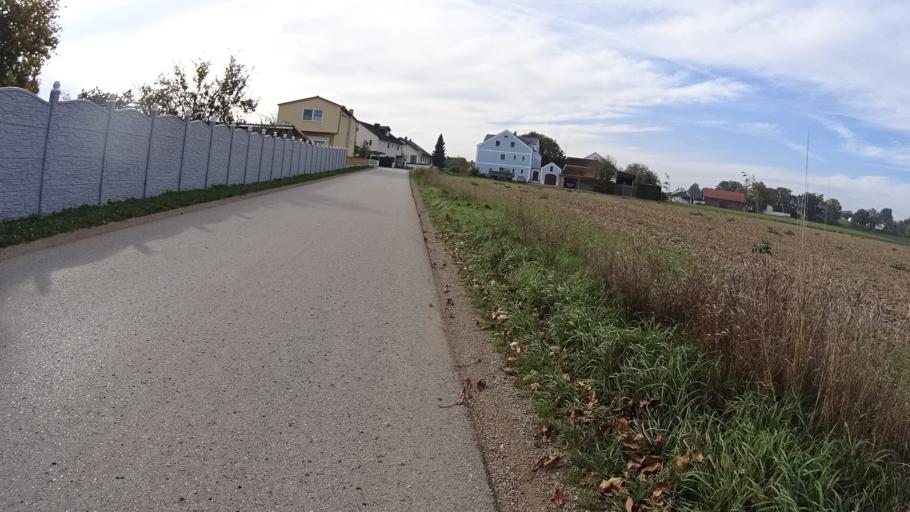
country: DE
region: Bavaria
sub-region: Upper Bavaria
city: Buxheim
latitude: 48.8253
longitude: 11.2807
